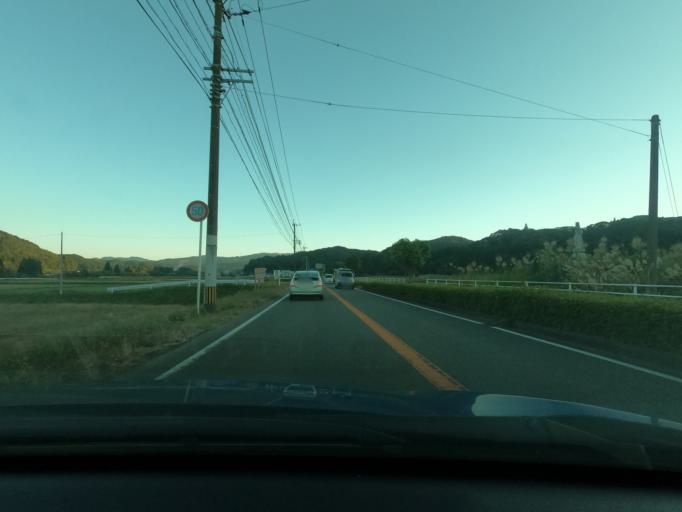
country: JP
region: Kagoshima
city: Satsumasendai
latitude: 31.8028
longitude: 130.3983
